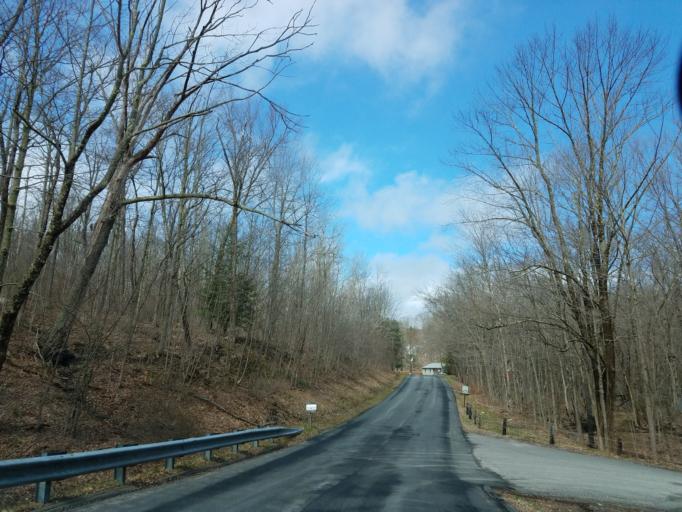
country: US
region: Connecticut
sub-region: Litchfield County
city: West Torrington
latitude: 41.7816
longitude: -73.1603
